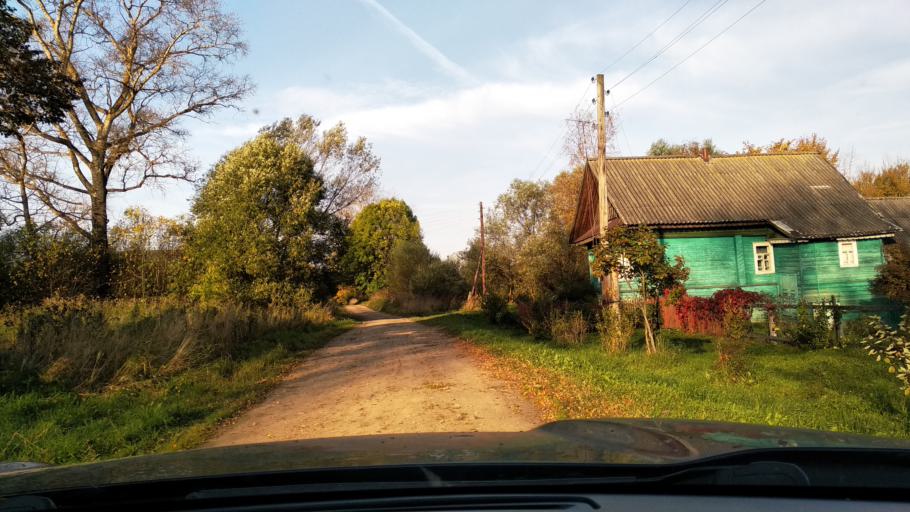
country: RU
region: Tverskaya
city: Krasnyy Kholm
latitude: 58.0094
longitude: 37.1912
